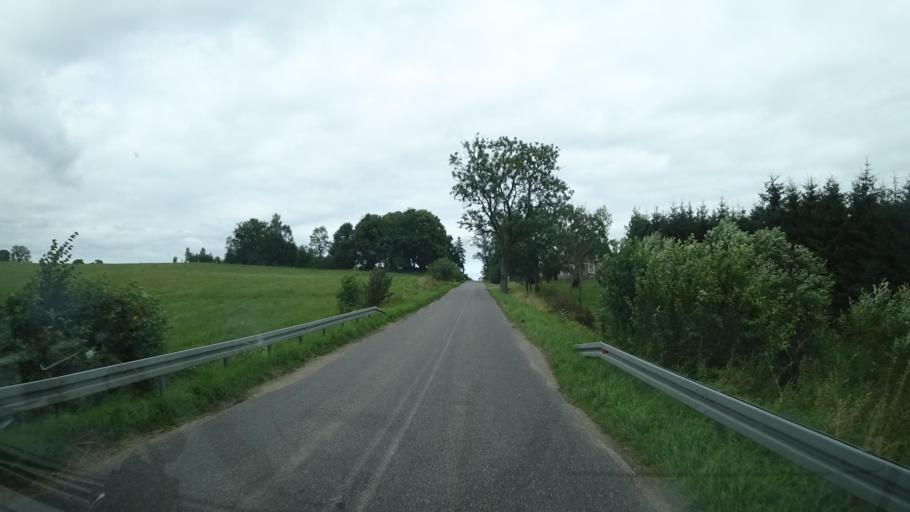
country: PL
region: Podlasie
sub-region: Powiat suwalski
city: Filipow
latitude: 54.2851
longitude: 22.5497
